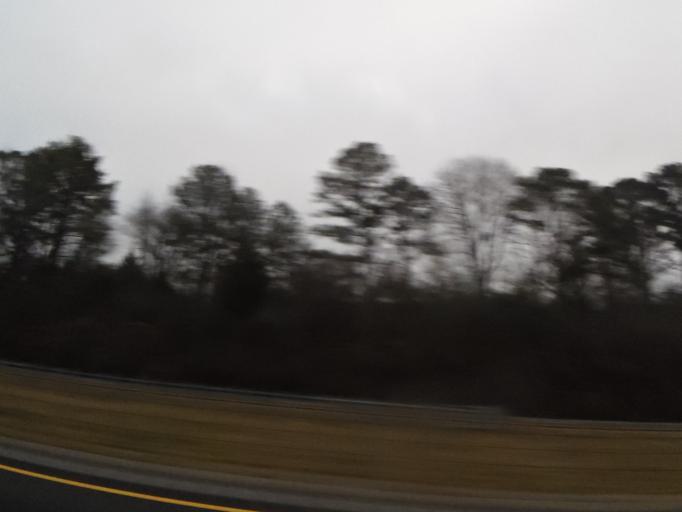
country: US
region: Alabama
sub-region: Cullman County
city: Cullman
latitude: 34.1885
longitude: -86.8788
